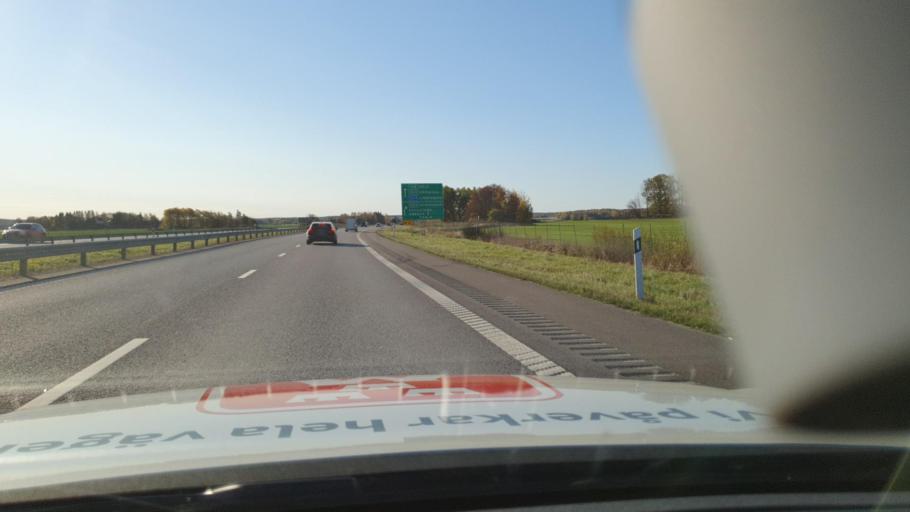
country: SE
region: Vaestmanland
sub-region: Arboga Kommun
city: Arboga
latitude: 59.4440
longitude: 15.8987
